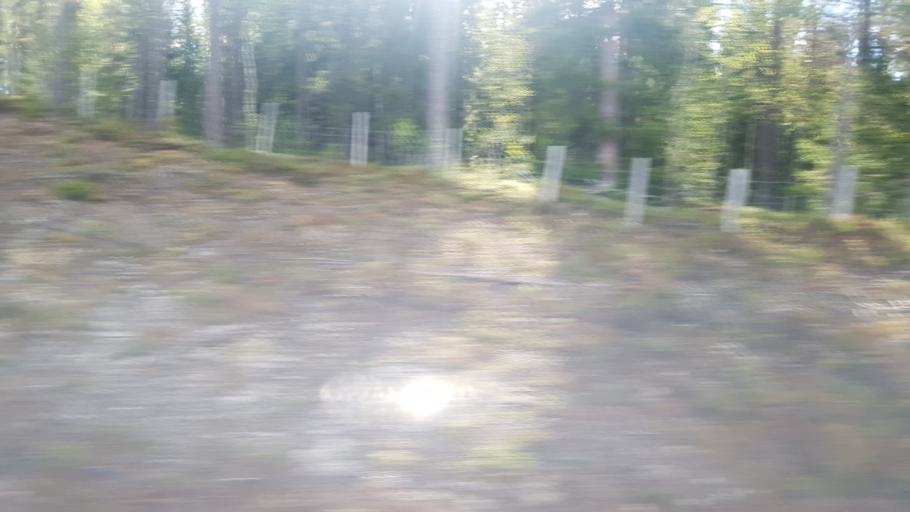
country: NO
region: Sor-Trondelag
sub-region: Rennebu
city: Berkak
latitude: 62.9092
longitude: 10.1284
